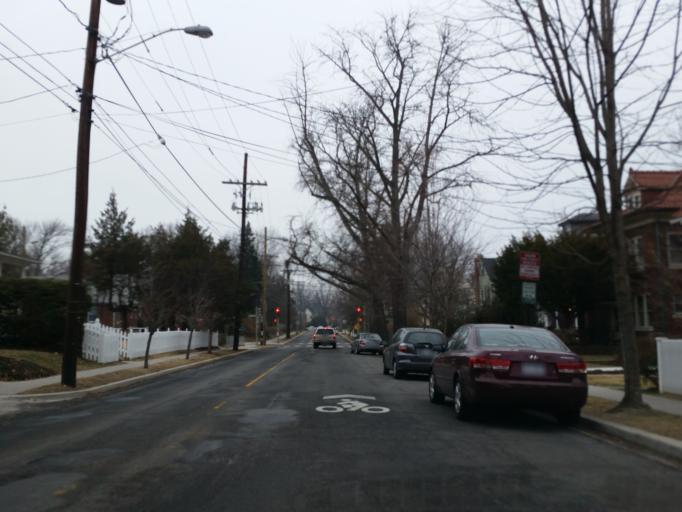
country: US
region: Maryland
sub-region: Montgomery County
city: Chevy Chase Village
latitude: 38.9623
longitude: -77.0803
